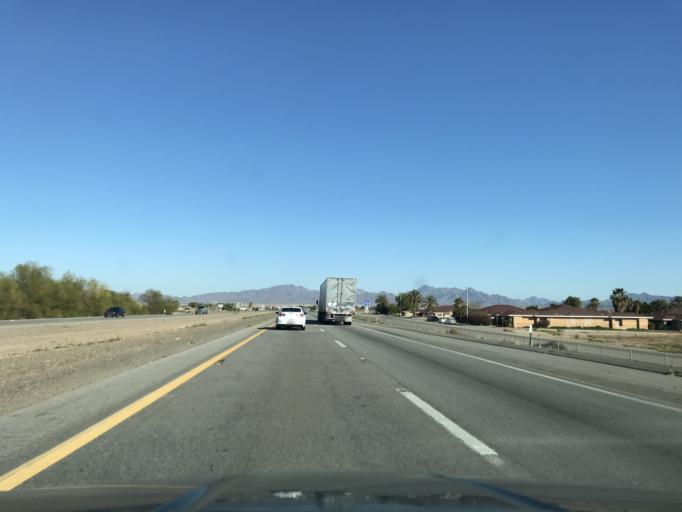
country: US
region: California
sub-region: Riverside County
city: Blythe
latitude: 33.6067
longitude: -114.5666
